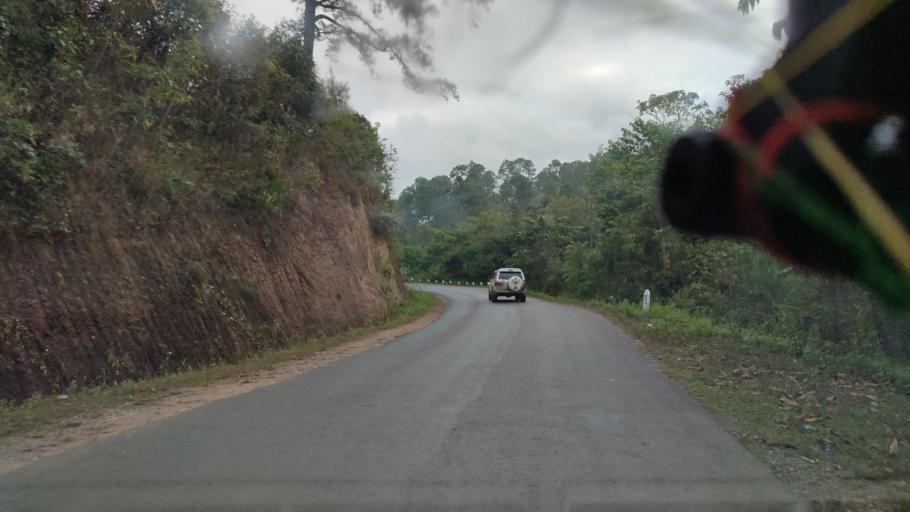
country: MM
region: Shan
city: Taunggyi
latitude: 21.1668
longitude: 97.6034
